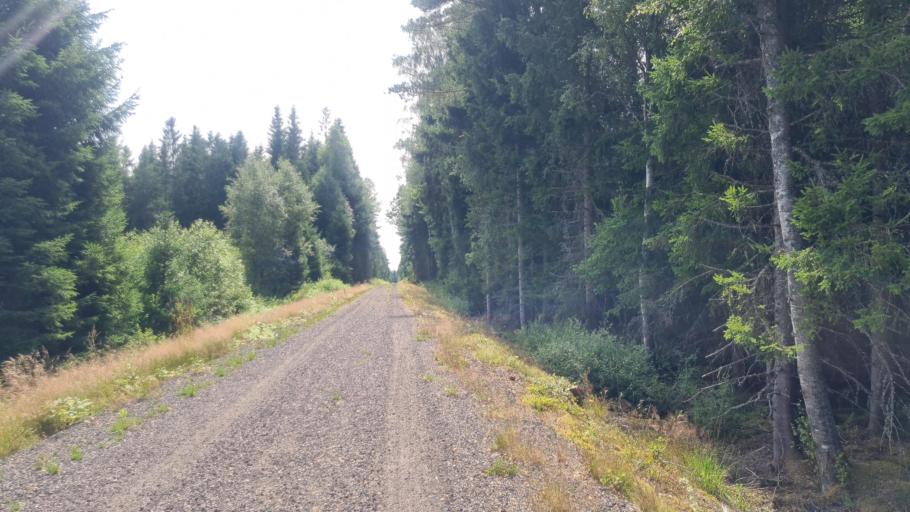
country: SE
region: Kronoberg
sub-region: Ljungby Kommun
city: Lagan
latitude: 56.9478
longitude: 13.9644
